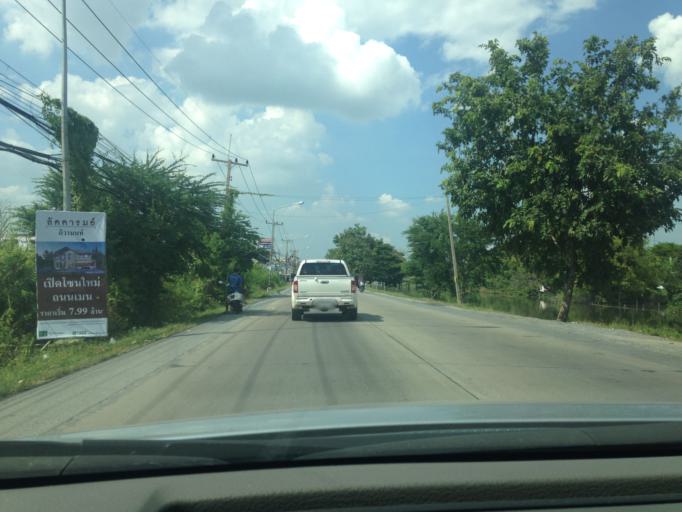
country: TH
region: Phra Nakhon Si Ayutthaya
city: Ban Bang Kadi Pathum Thani
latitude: 13.9862
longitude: 100.5995
